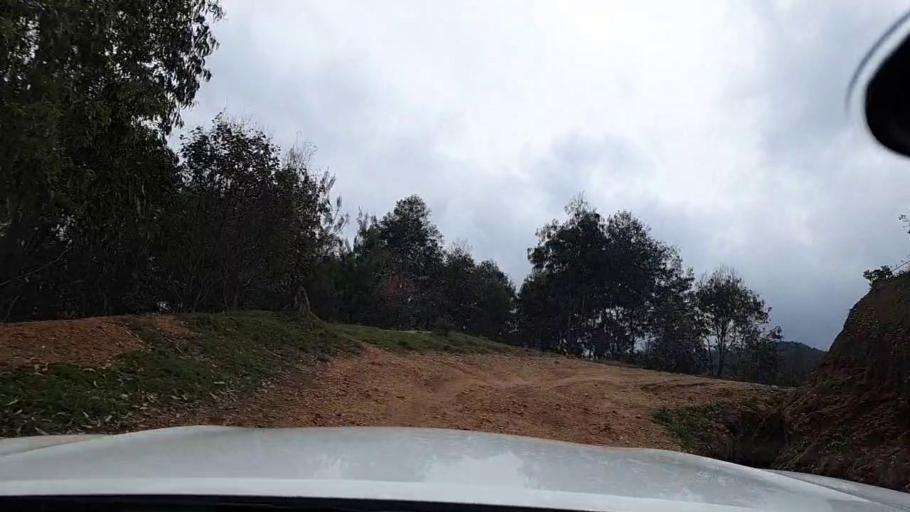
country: RW
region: Western Province
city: Kibuye
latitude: -2.2003
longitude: 29.3207
